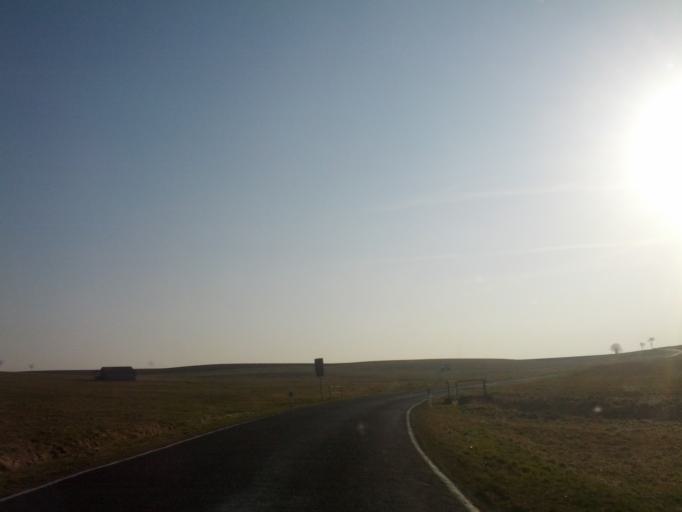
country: DE
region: Thuringia
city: Bischofroda
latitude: 51.0382
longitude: 10.3915
